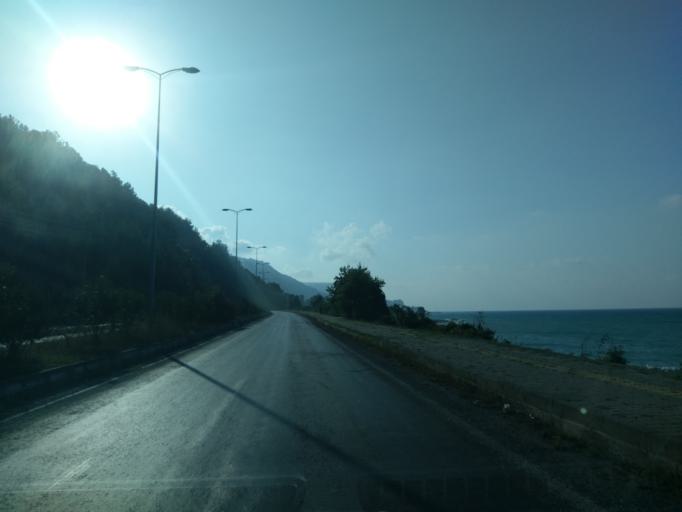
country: TR
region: Kastamonu
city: Catalzeytin
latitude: 41.9558
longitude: 34.1994
